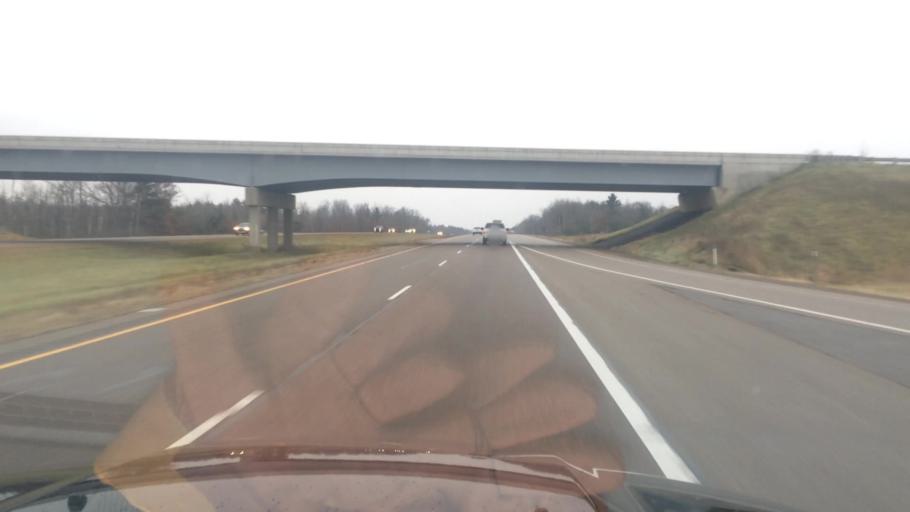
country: US
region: Wisconsin
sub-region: Portage County
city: Stevens Point
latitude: 44.5957
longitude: -89.6143
